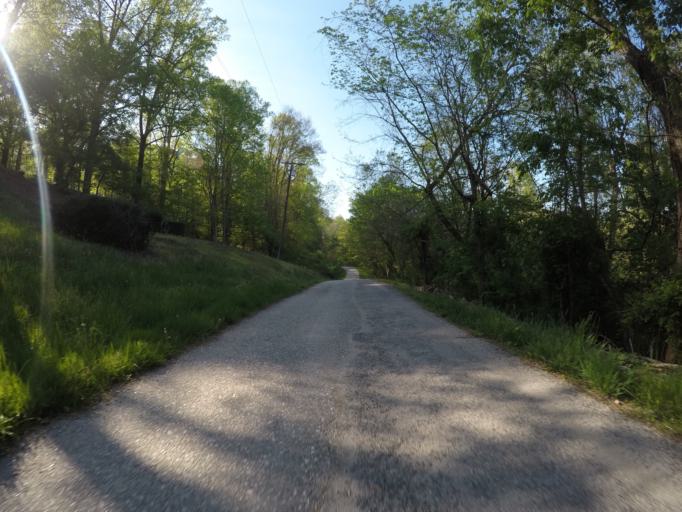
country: US
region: West Virginia
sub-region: Kanawha County
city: Charleston
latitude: 38.3890
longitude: -81.6076
